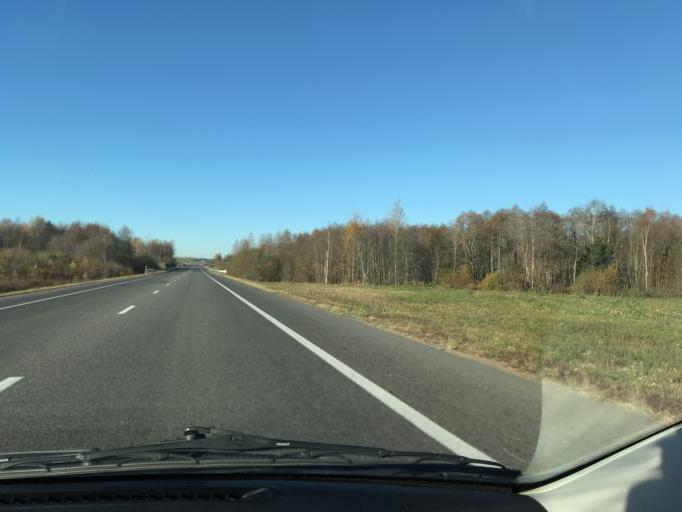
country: BY
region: Vitebsk
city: Vitebsk
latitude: 55.1042
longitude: 30.2109
